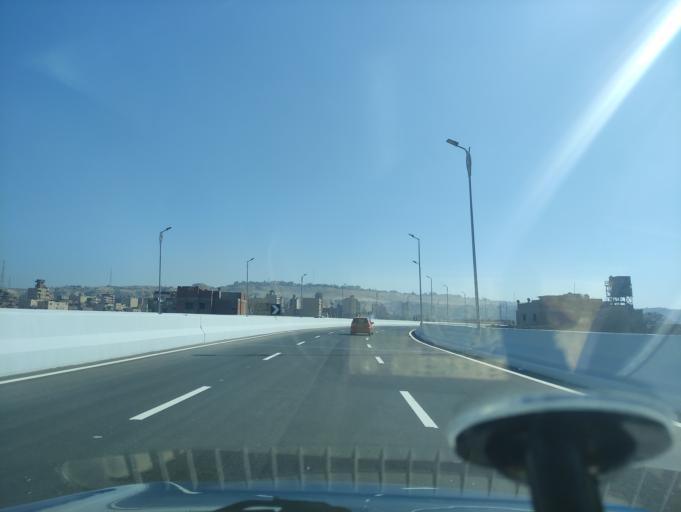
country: EG
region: Al Jizah
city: Al Jizah
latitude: 30.0080
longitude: 31.2569
